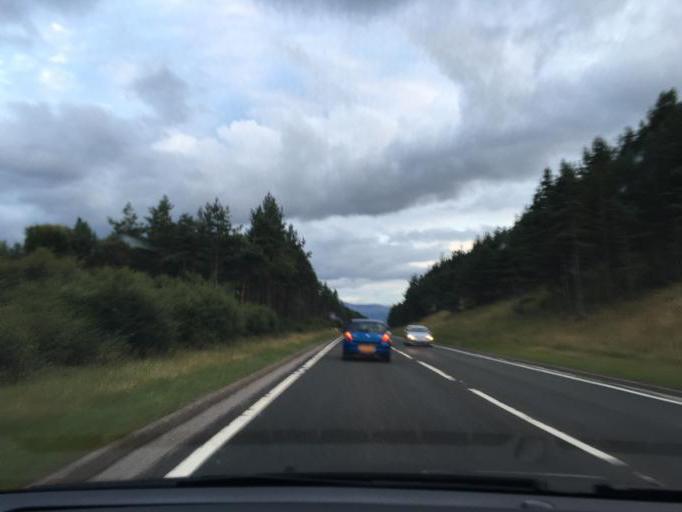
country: GB
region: Scotland
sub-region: Highland
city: Aviemore
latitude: 57.2569
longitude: -3.8089
